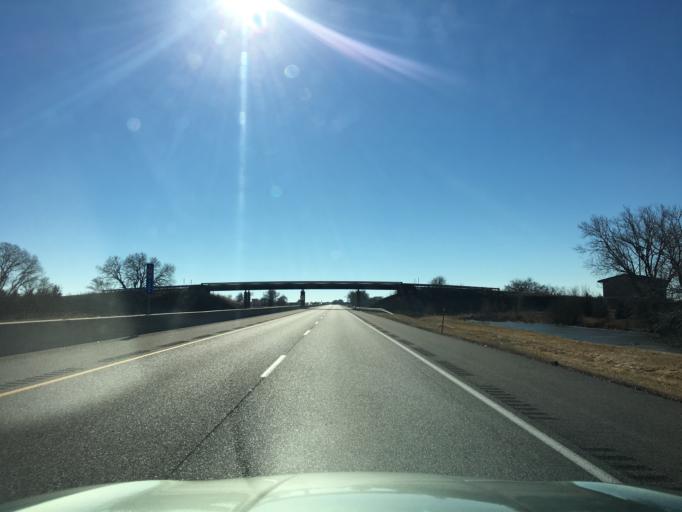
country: US
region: Kansas
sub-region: Sumner County
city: Mulvane
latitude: 37.4662
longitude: -97.3227
